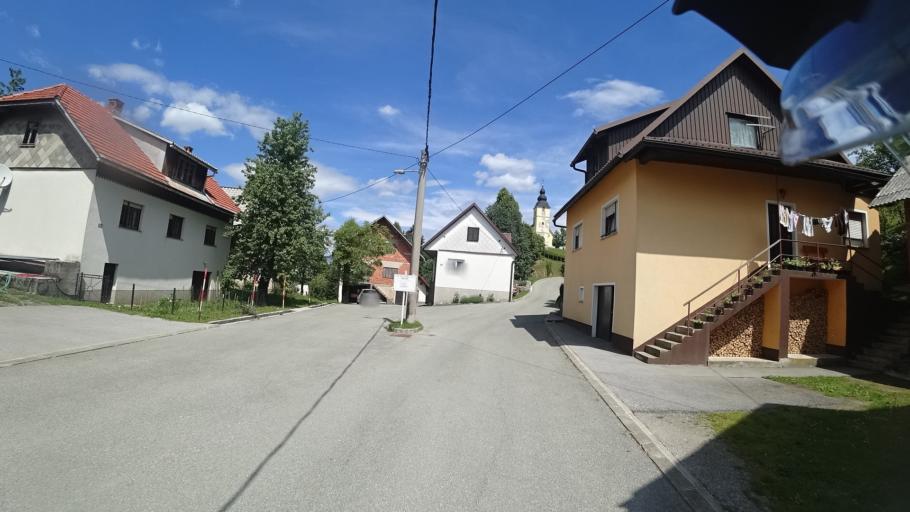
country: SI
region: Osilnica
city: Osilnica
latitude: 45.5142
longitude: 14.6748
